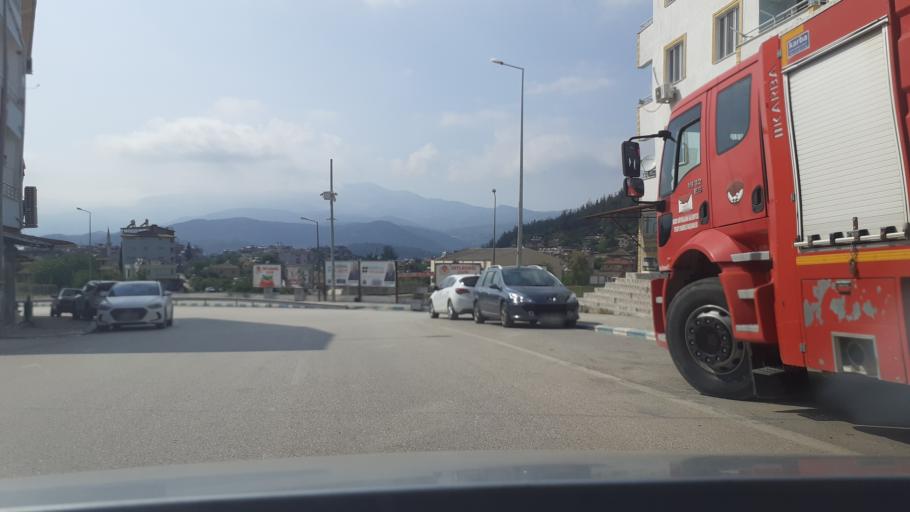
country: TR
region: Hatay
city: Yayladagi
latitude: 35.9003
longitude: 36.0708
